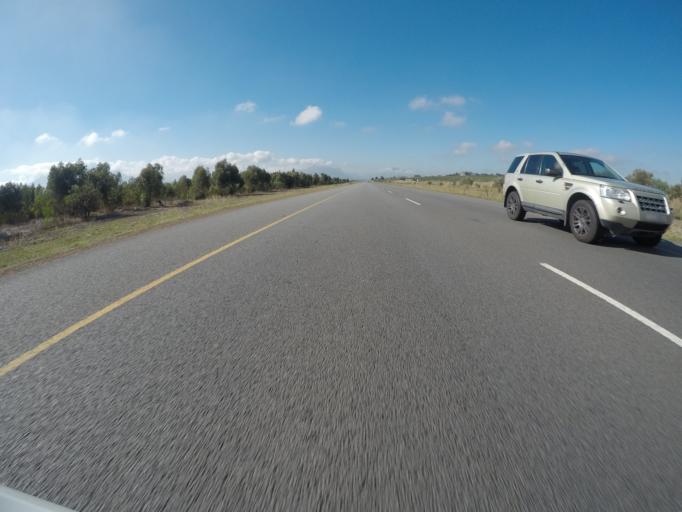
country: ZA
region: Western Cape
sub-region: City of Cape Town
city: Kraaifontein
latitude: -33.8520
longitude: 18.8062
